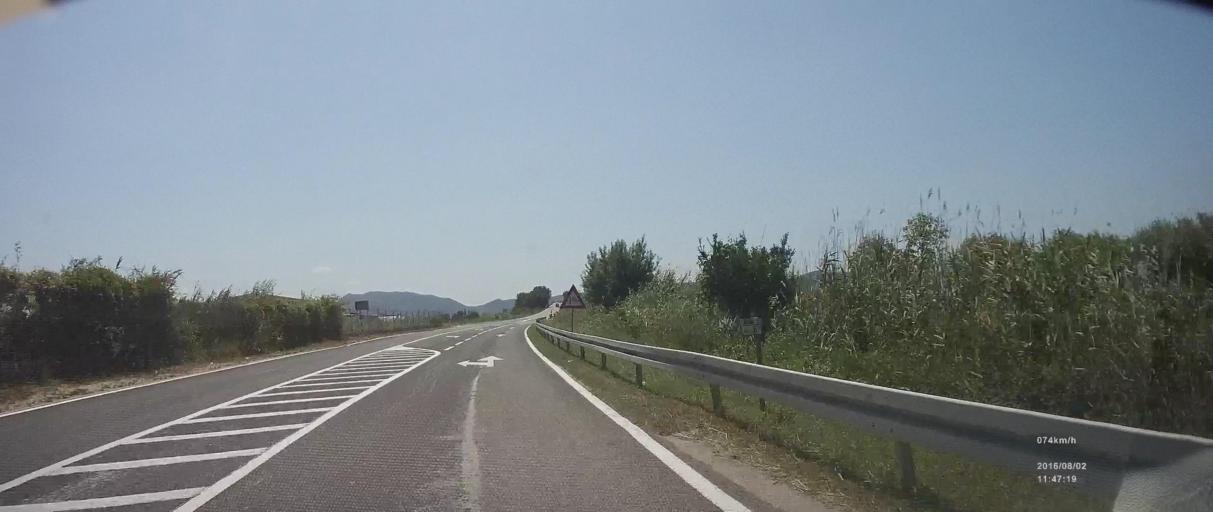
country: HR
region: Dubrovacko-Neretvanska
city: Komin
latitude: 43.0452
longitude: 17.4814
